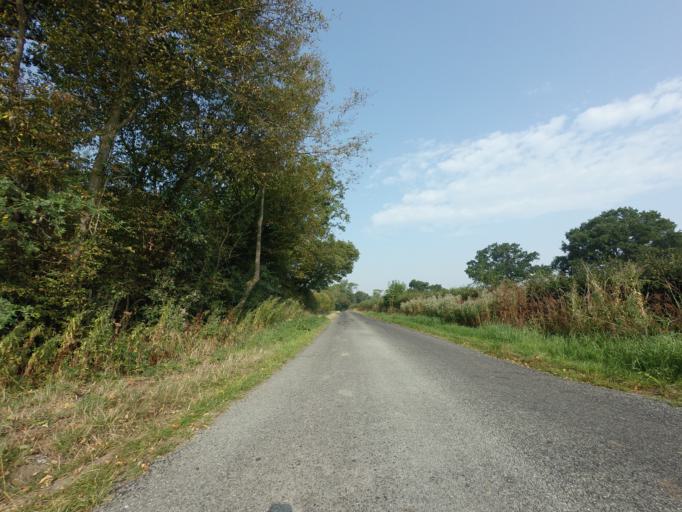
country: GB
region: England
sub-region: Kent
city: Headcorn
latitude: 51.1279
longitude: 0.6591
